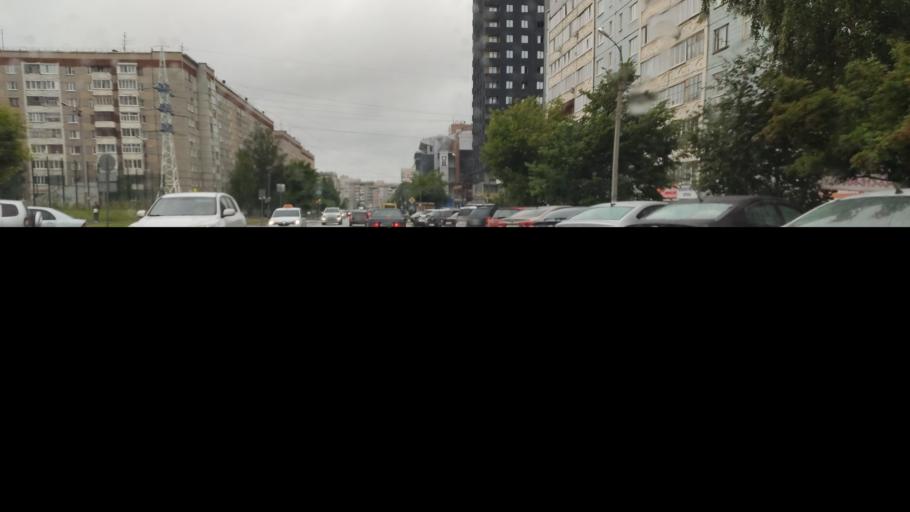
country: RU
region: Udmurtiya
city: Izhevsk
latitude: 56.8758
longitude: 53.2156
